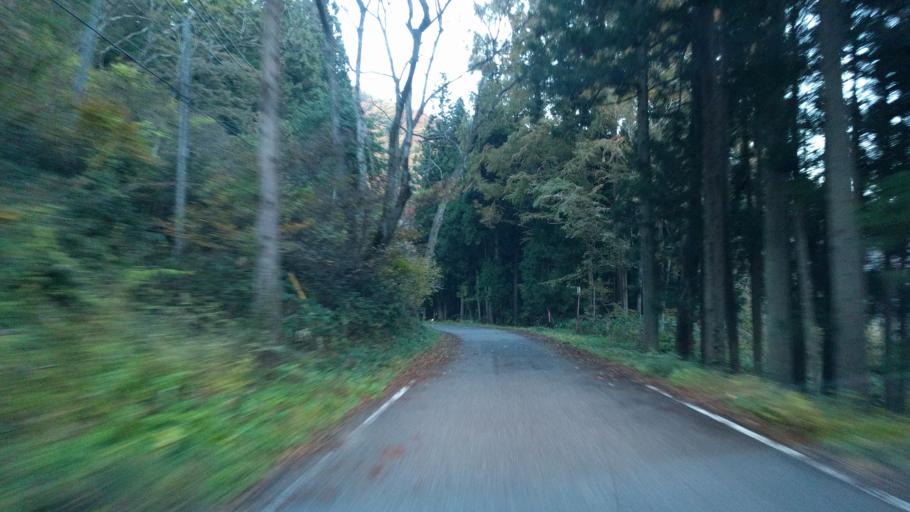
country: JP
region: Fukushima
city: Kitakata
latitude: 37.5057
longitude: 139.6822
